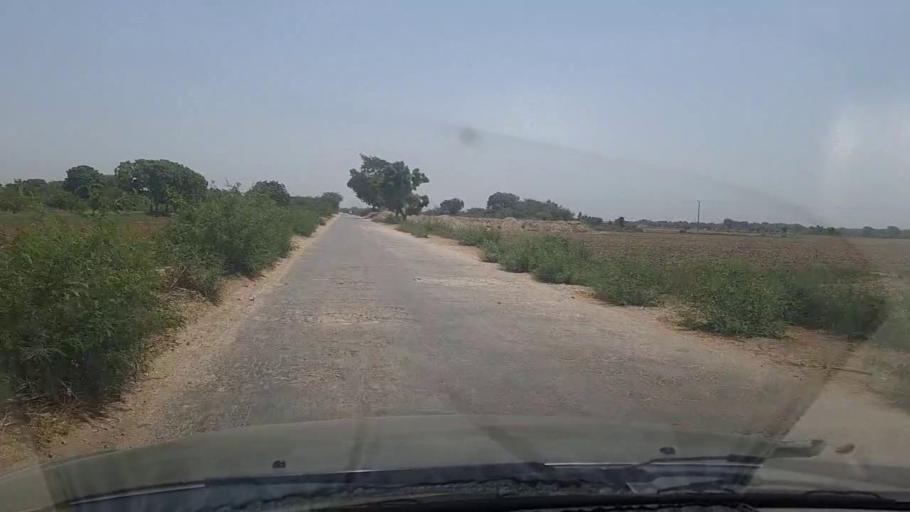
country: PK
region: Sindh
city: Tando Muhammad Khan
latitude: 25.2729
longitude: 68.6286
